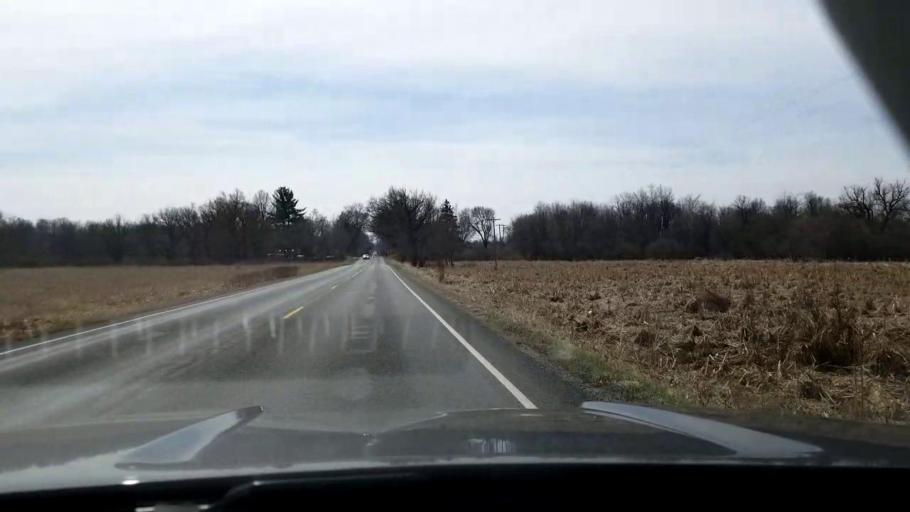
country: US
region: Michigan
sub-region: Jackson County
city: Spring Arbor
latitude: 42.2052
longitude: -84.5211
